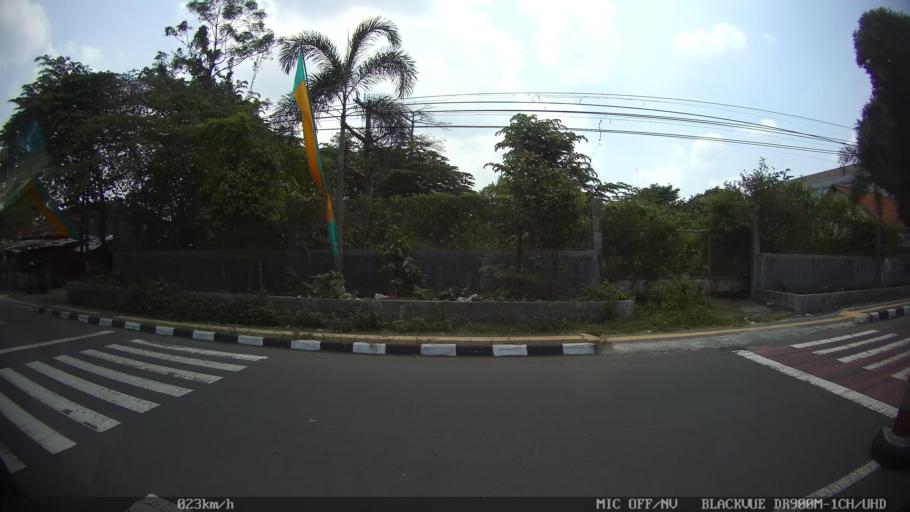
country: ID
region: Daerah Istimewa Yogyakarta
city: Yogyakarta
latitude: -7.8106
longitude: 110.4015
